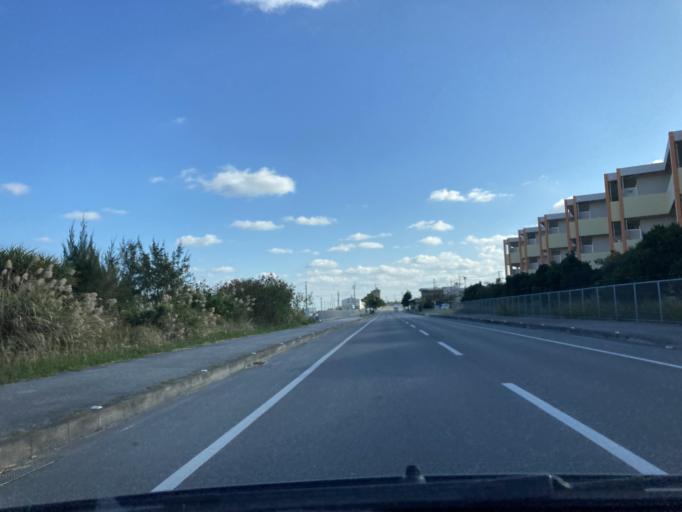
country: JP
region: Okinawa
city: Katsuren-haebaru
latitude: 26.3116
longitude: 127.9196
